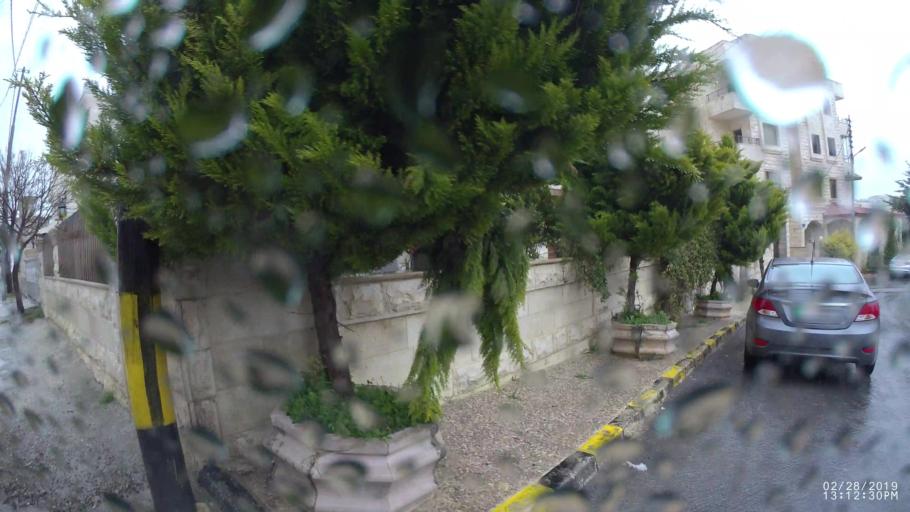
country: JO
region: Amman
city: Al Jubayhah
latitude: 32.0219
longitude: 35.8850
